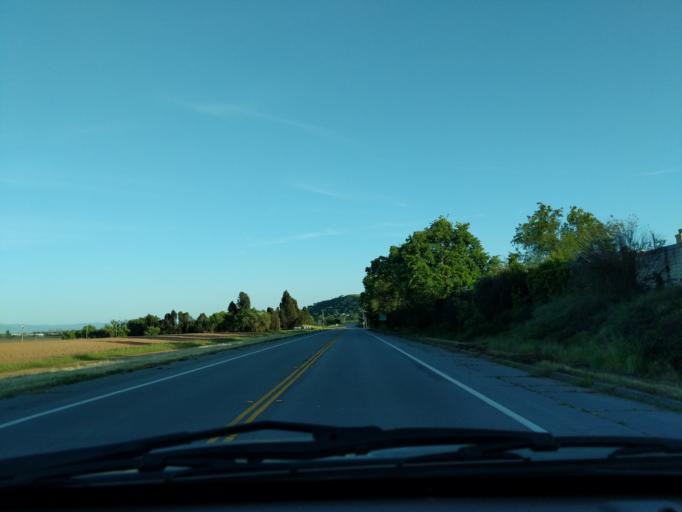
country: US
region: California
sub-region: Santa Clara County
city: Gilroy
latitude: 36.9784
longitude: -121.5696
